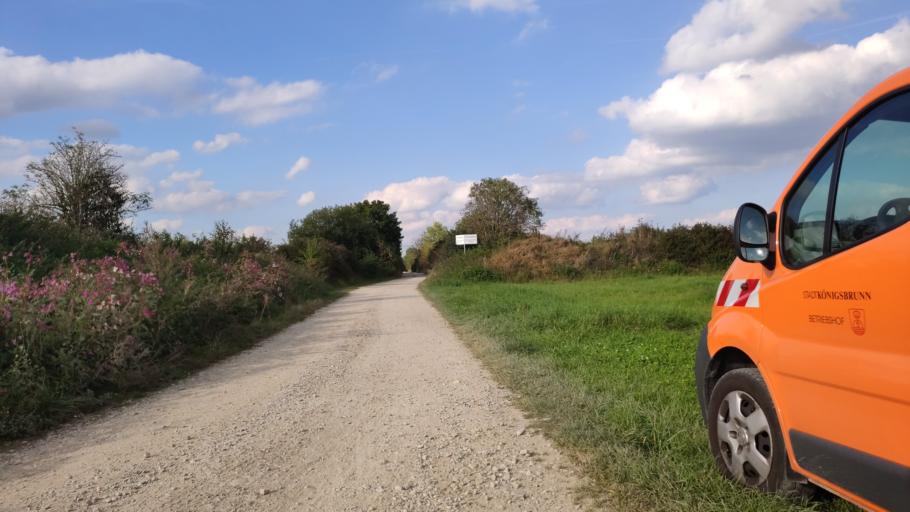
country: DE
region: Bavaria
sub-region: Swabia
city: Oberottmarshausen
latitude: 48.2244
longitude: 10.8748
